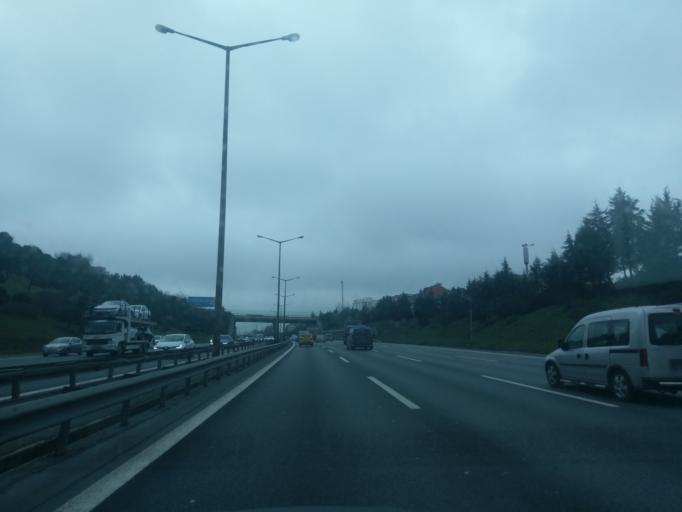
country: TR
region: Istanbul
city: Sultangazi
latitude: 41.0914
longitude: 28.8992
